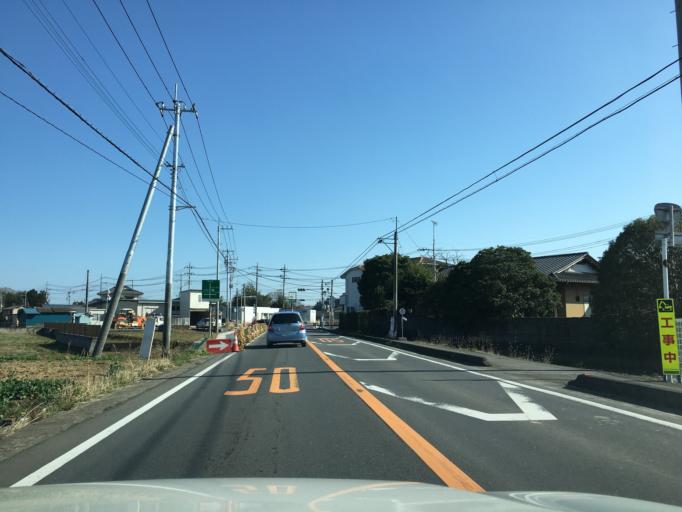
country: JP
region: Ibaraki
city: Omiya
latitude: 36.4963
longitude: 140.3724
